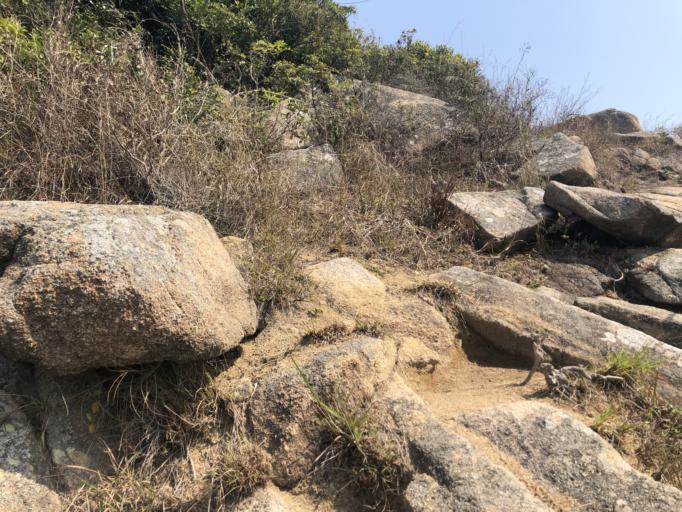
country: HK
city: Sok Kwu Wan
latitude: 22.1674
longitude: 114.2528
